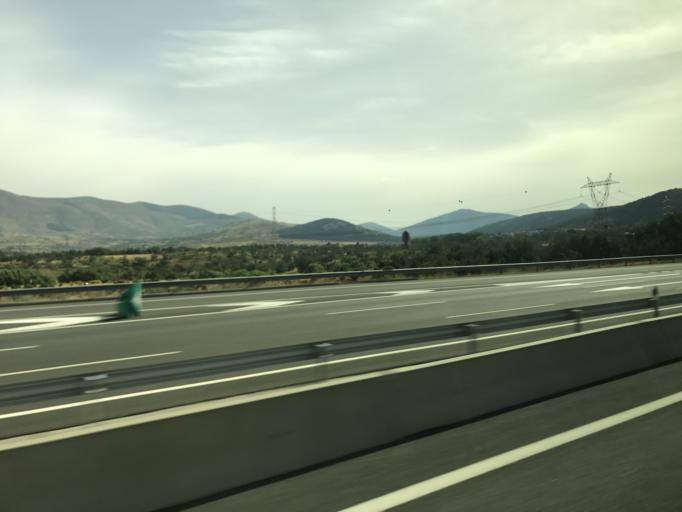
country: ES
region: Castille and Leon
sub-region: Provincia de Segovia
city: Otero de Herreros
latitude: 40.7352
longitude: -4.2051
